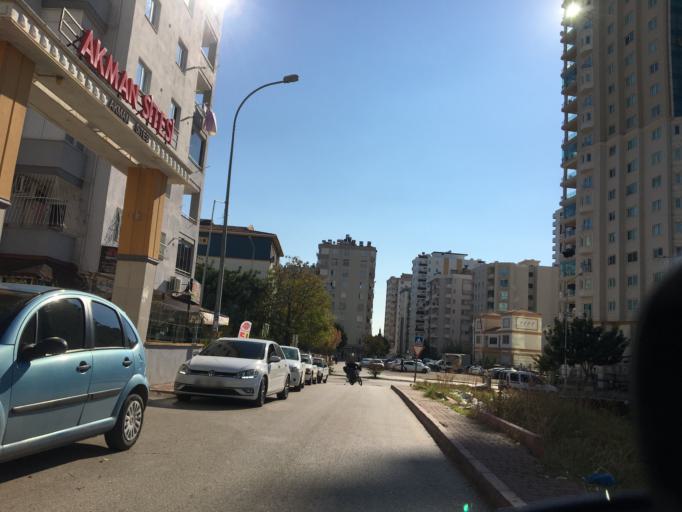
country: TR
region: Adana
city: Seyhan
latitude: 37.0182
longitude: 35.2871
